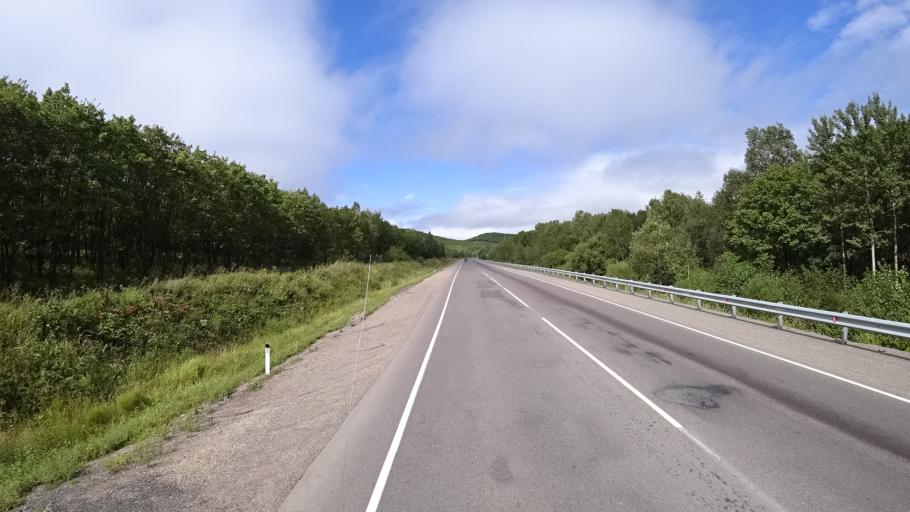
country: RU
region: Primorskiy
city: Lyalichi
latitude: 44.1125
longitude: 132.4198
